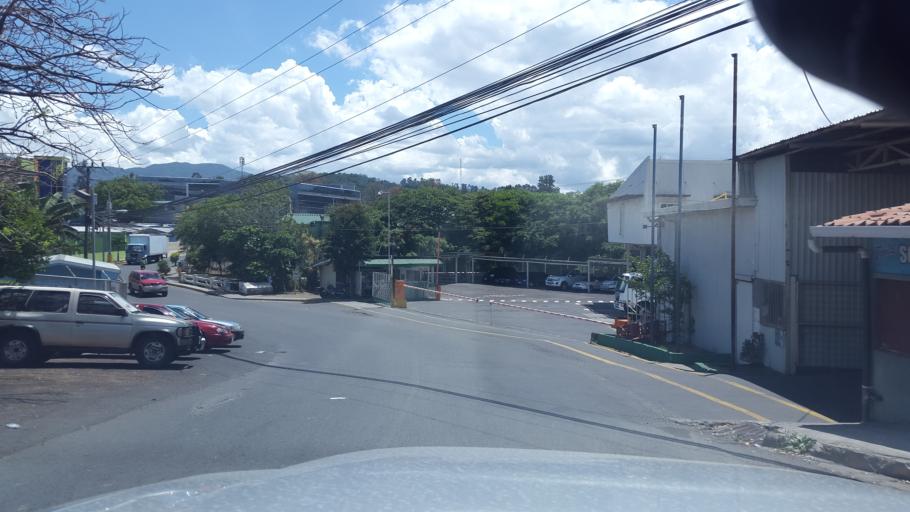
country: CR
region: San Jose
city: Curridabat
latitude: 9.9165
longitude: -84.0276
